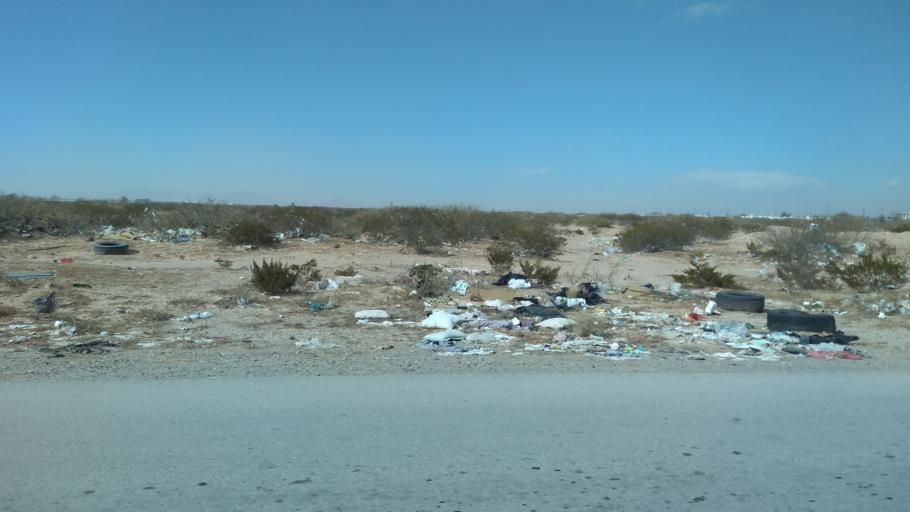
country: US
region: Texas
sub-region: El Paso County
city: San Elizario
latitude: 31.5727
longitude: -106.3311
